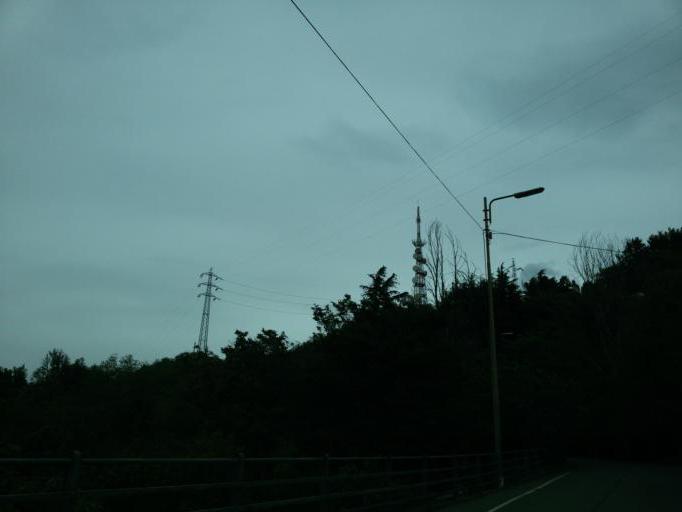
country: IT
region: Liguria
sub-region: Provincia di Genova
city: Genoa
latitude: 44.4295
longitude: 8.9090
